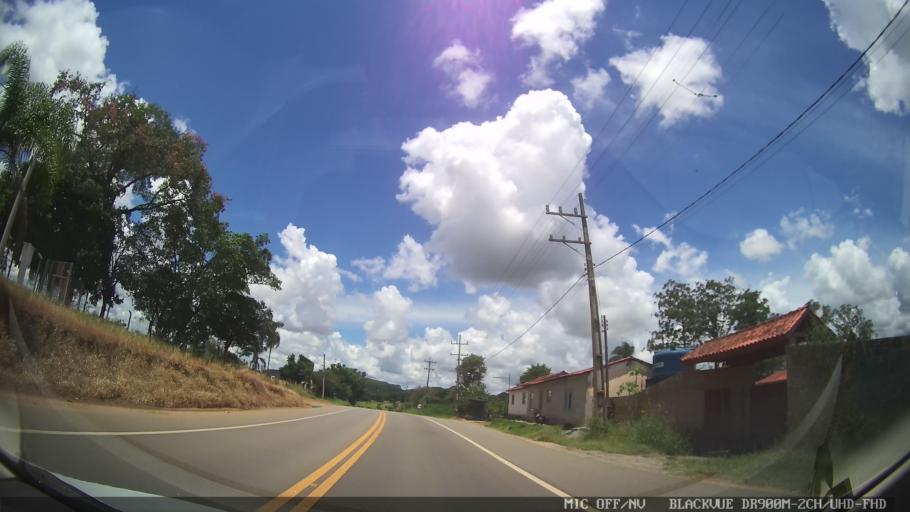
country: BR
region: Sao Paulo
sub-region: Braganca Paulista
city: Braganca Paulista
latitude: -22.8916
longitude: -46.6055
